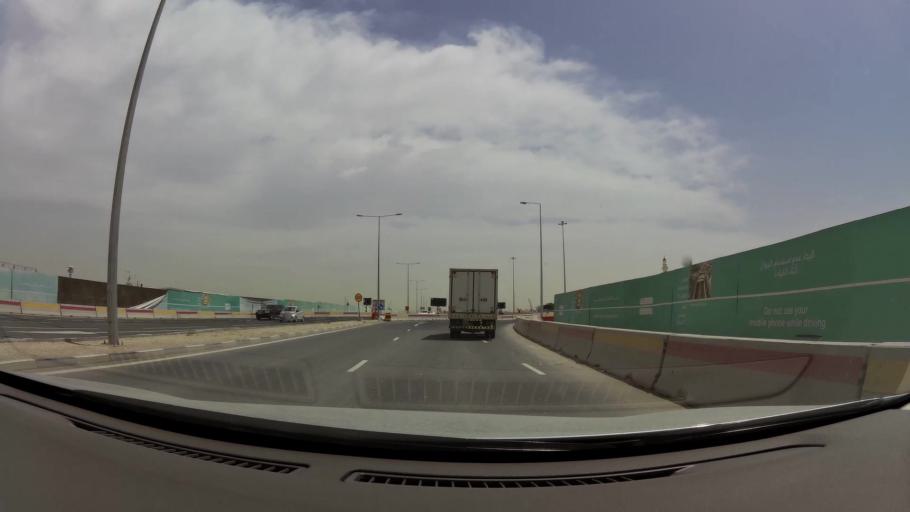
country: QA
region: Baladiyat ar Rayyan
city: Ar Rayyan
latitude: 25.3062
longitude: 51.4134
